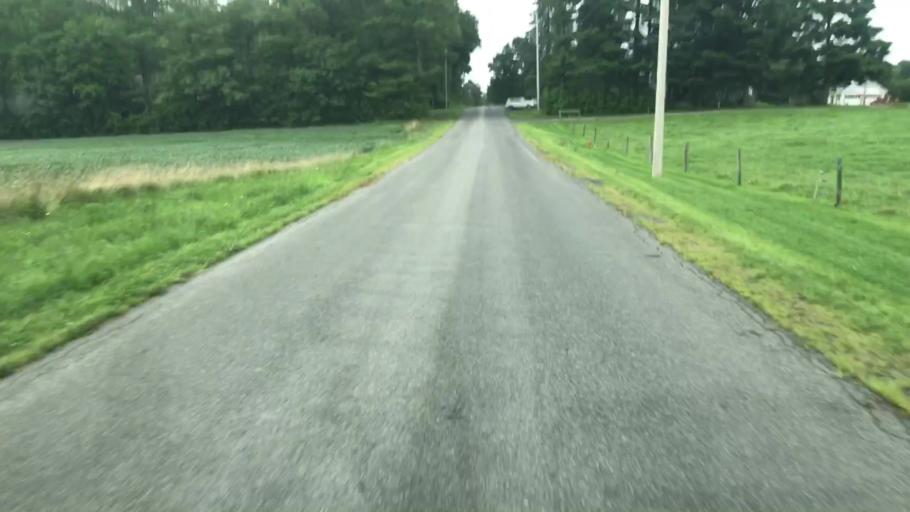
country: US
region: New York
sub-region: Cayuga County
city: Melrose Park
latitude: 42.9582
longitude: -76.5068
